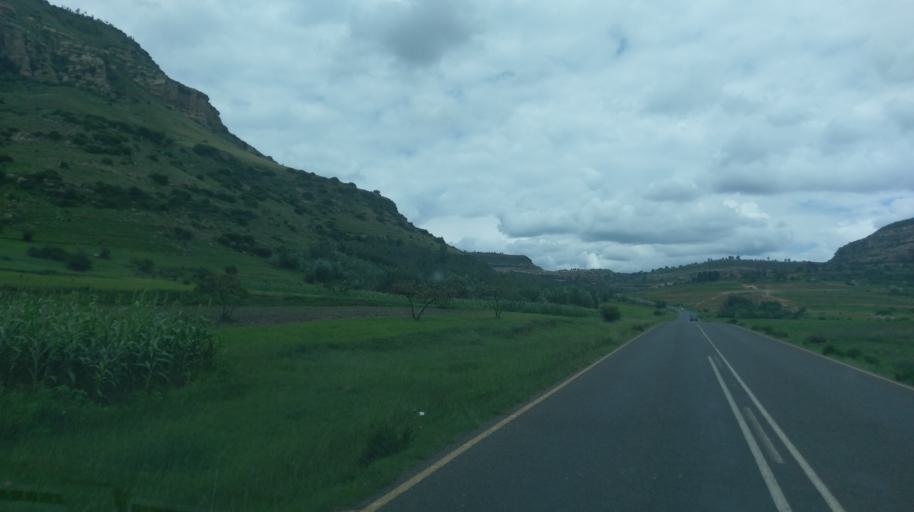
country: LS
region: Leribe
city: Leribe
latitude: -28.9757
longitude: 28.1767
